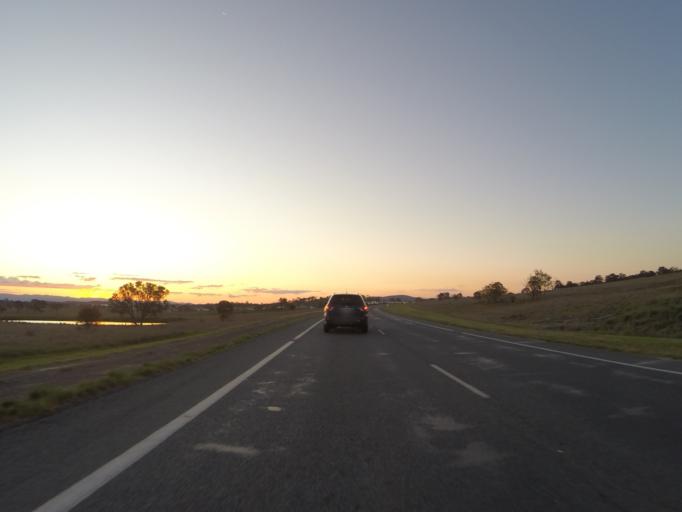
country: AU
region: Australian Capital Territory
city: Kaleen
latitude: -35.2112
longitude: 149.1746
